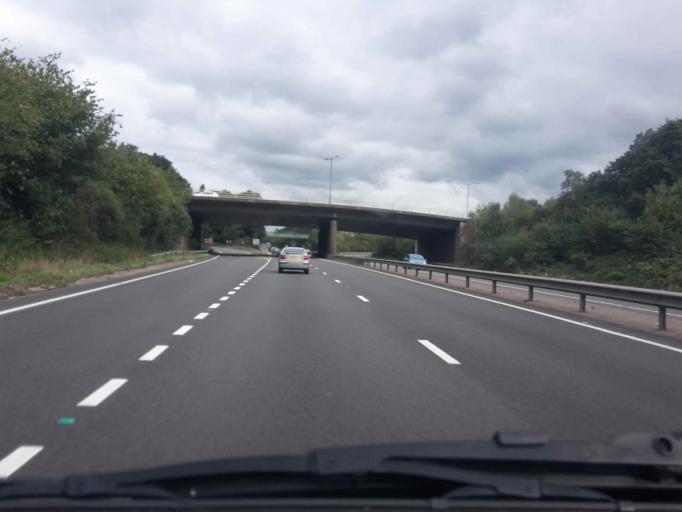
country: GB
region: England
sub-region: Hampshire
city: Farnborough
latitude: 51.2732
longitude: -0.7337
